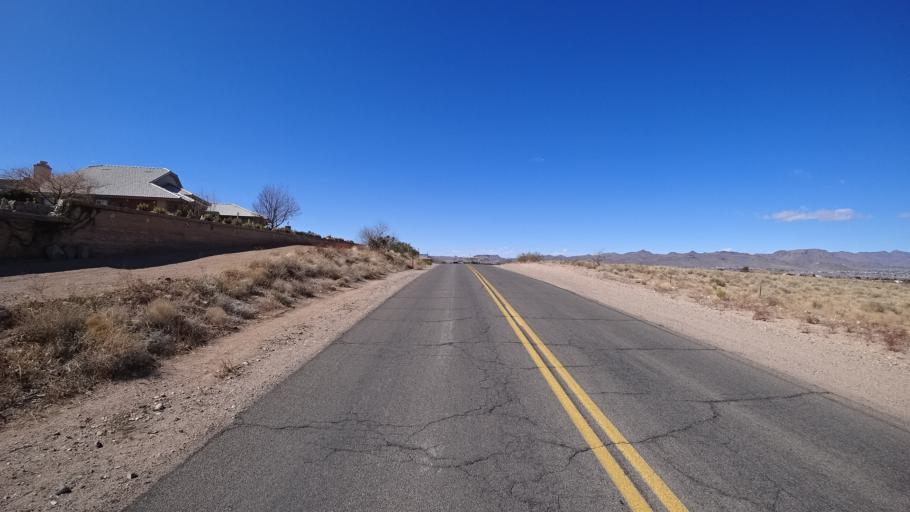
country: US
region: Arizona
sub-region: Mohave County
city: Kingman
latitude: 35.1958
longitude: -113.9915
